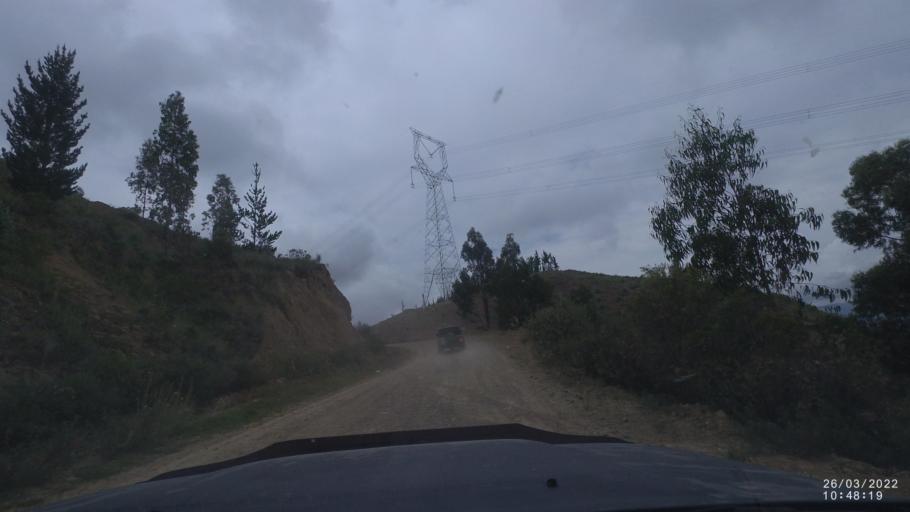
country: BO
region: Cochabamba
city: Tarata
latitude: -17.4951
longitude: -66.0448
